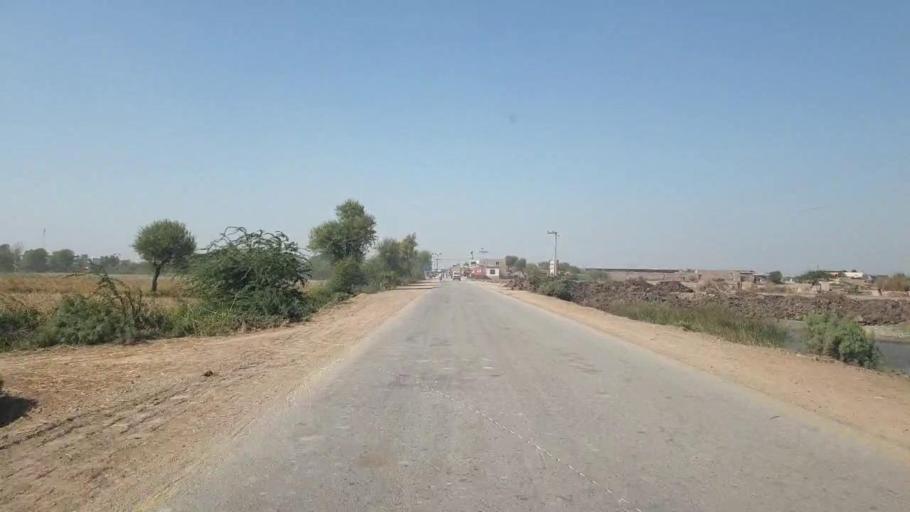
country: PK
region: Sindh
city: Rajo Khanani
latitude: 25.0587
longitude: 68.8018
